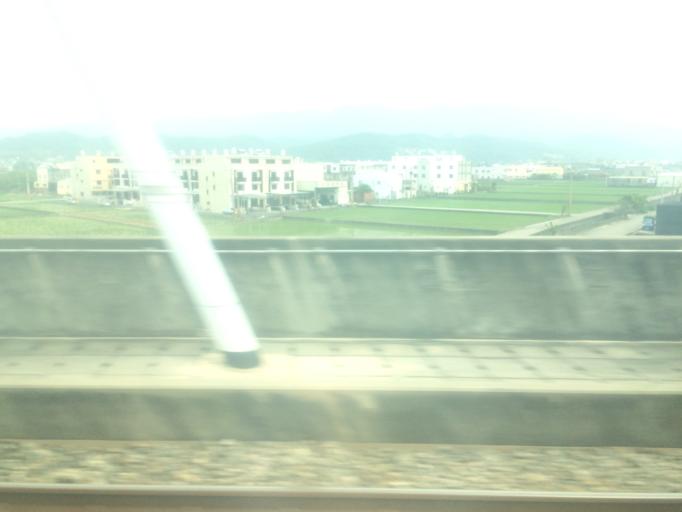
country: TW
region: Taiwan
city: Fengyuan
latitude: 24.3937
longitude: 120.6875
